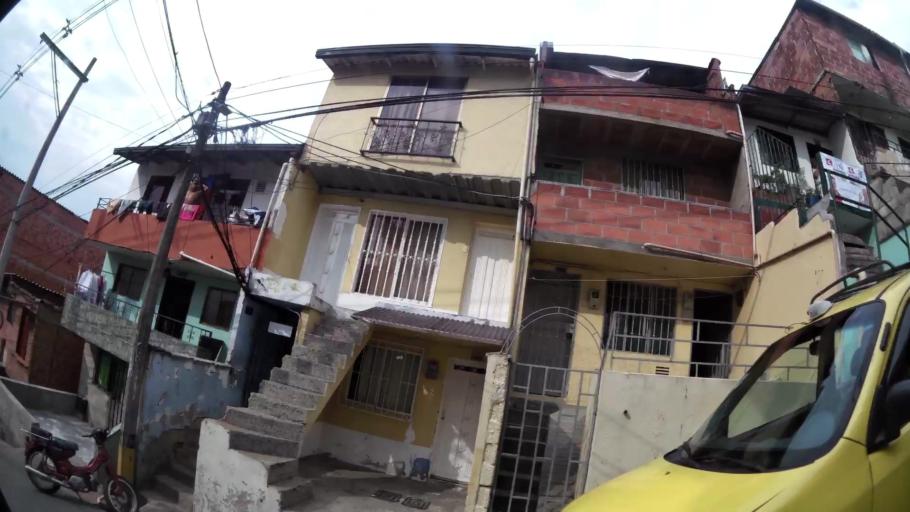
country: CO
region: Antioquia
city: Bello
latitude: 6.3006
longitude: -75.5529
